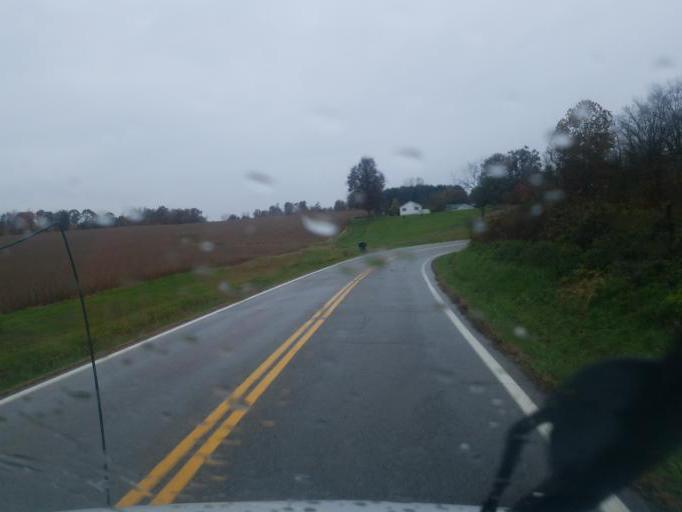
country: US
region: Ohio
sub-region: Washington County
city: Beverly
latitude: 39.4722
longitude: -81.7230
